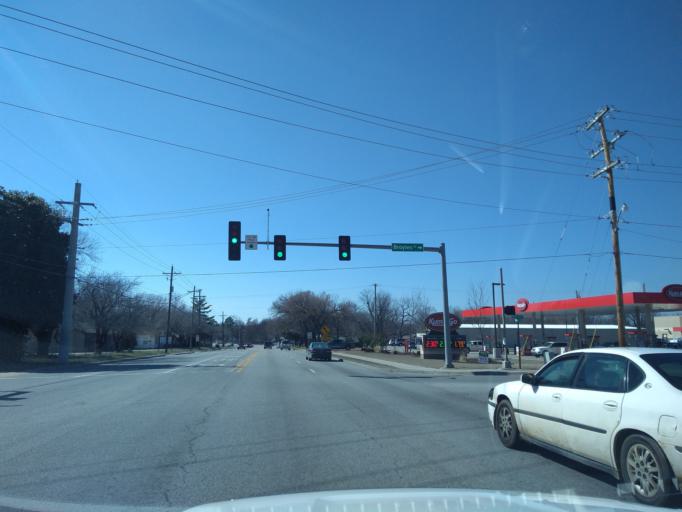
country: US
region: Arkansas
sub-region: Washington County
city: Farmington
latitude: 36.0427
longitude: -94.2359
